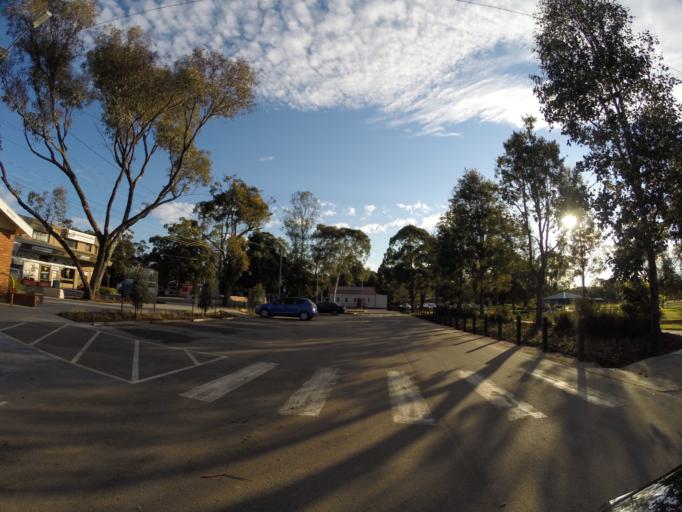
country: AU
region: New South Wales
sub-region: Fairfield
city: Horsley Park
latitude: -33.8410
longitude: 150.8468
